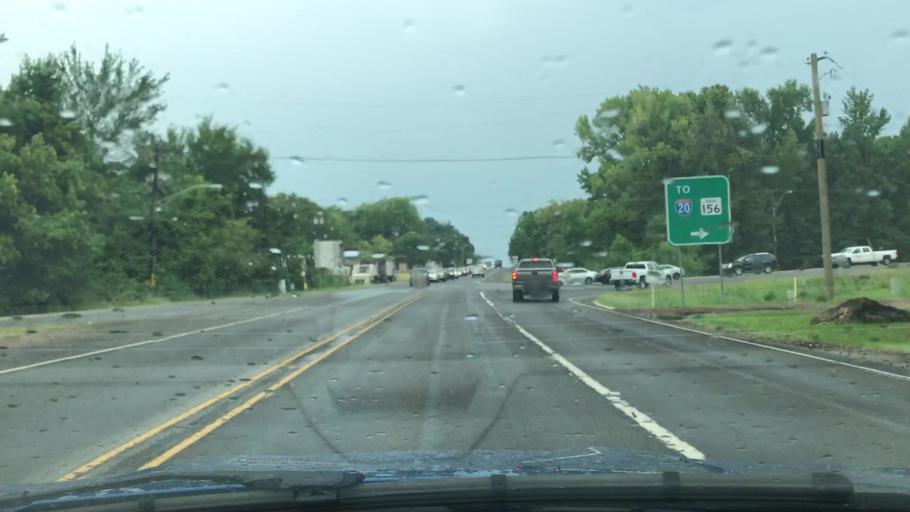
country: US
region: Texas
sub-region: Harrison County
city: Waskom
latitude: 32.4766
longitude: -94.0530
